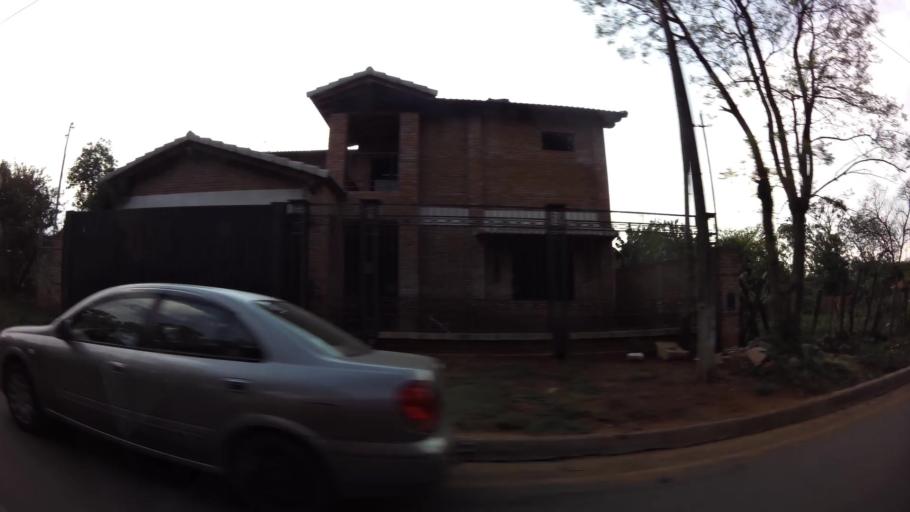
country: PY
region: Central
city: Fernando de la Mora
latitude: -25.3642
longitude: -57.5234
